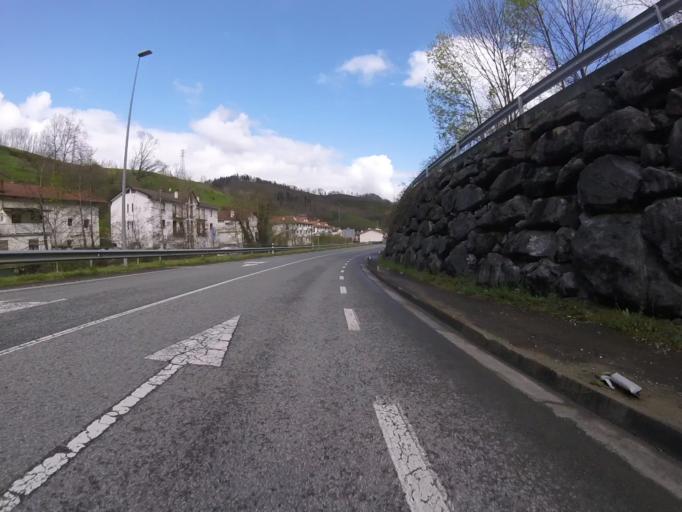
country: ES
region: Basque Country
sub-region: Provincia de Guipuzcoa
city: Amezqueta
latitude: 43.0507
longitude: -2.0882
